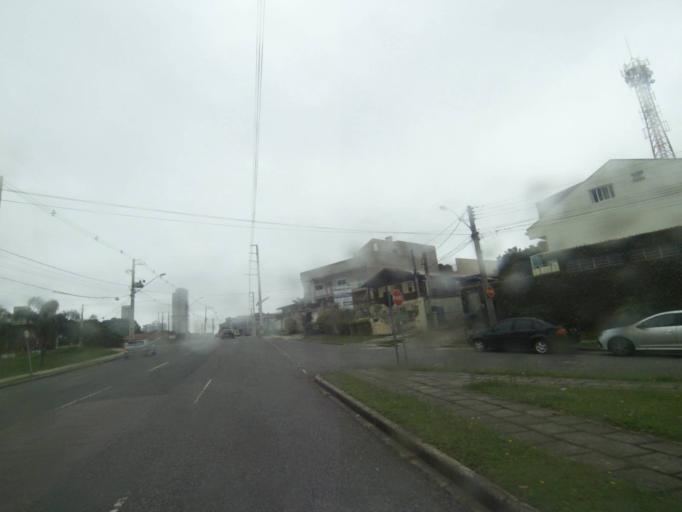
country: BR
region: Parana
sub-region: Curitiba
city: Curitiba
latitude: -25.4428
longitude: -49.3465
